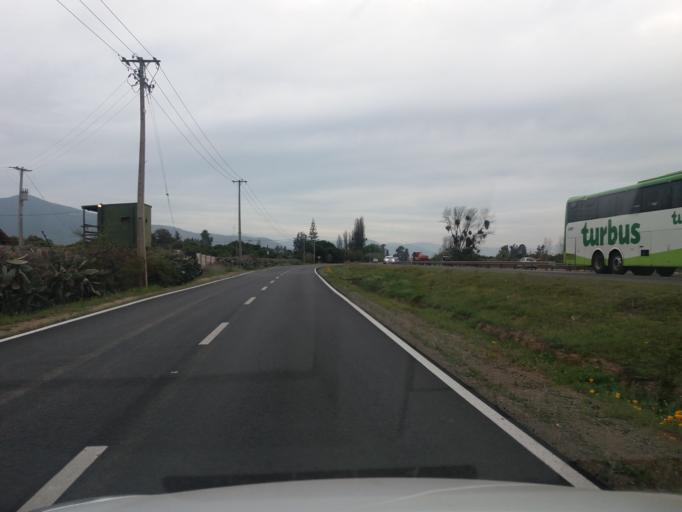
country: CL
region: Valparaiso
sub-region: Provincia de Quillota
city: Hacienda La Calera
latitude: -32.8260
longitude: -71.1342
